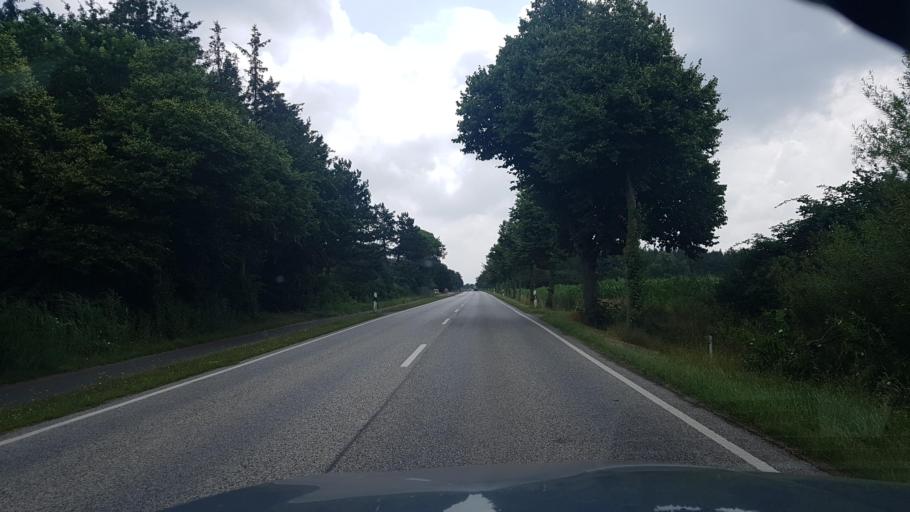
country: DE
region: Schleswig-Holstein
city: Tating
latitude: 54.3265
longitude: 8.7157
